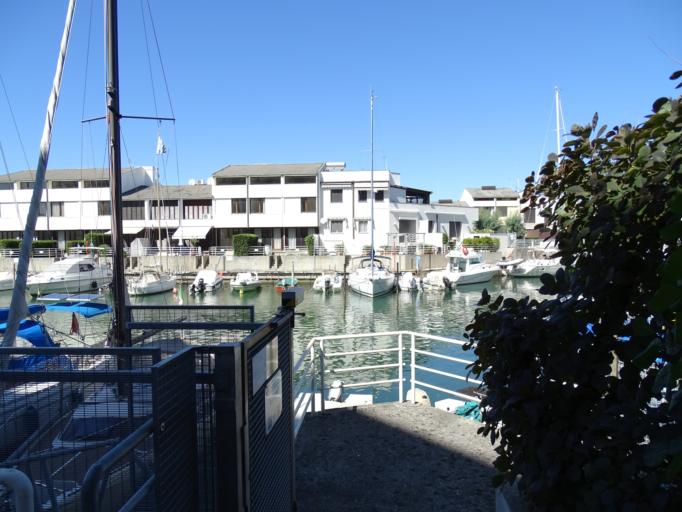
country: IT
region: Friuli Venezia Giulia
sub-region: Provincia di Udine
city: Lignano Sabbiadoro
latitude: 45.6961
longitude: 13.1487
